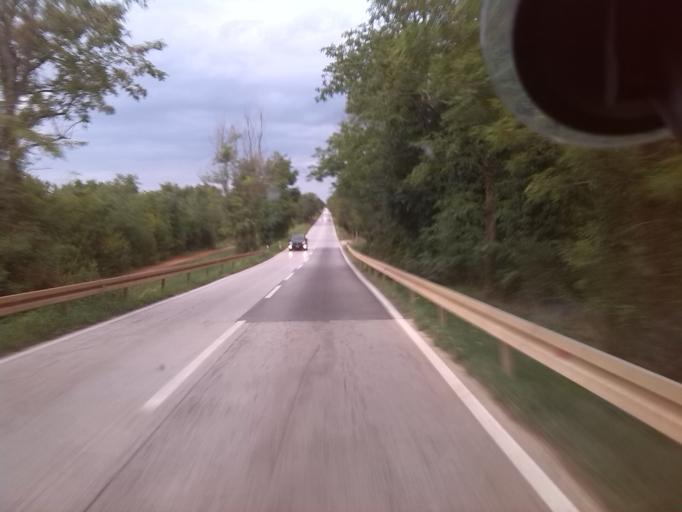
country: HR
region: Istarska
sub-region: Grad Porec
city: Porec
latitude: 45.2854
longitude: 13.6207
